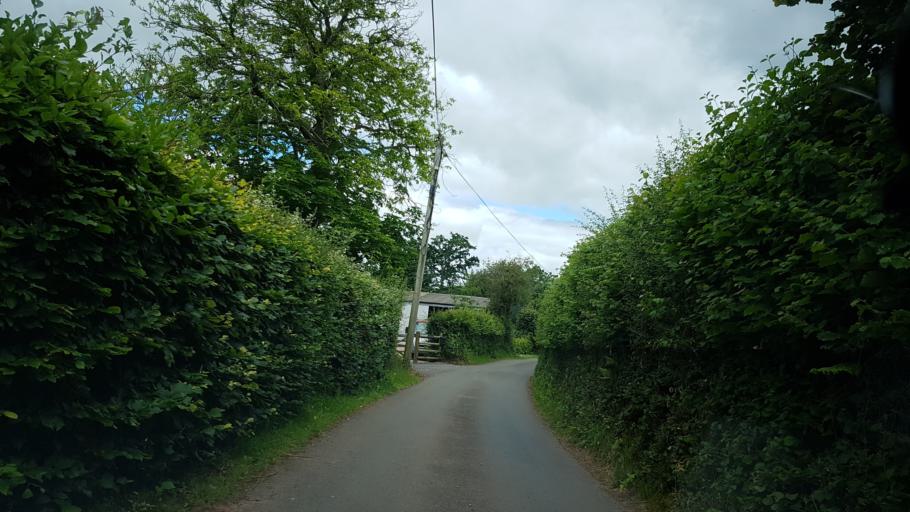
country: GB
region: Wales
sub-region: Monmouthshire
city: Llanarth
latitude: 51.8128
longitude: -2.8531
